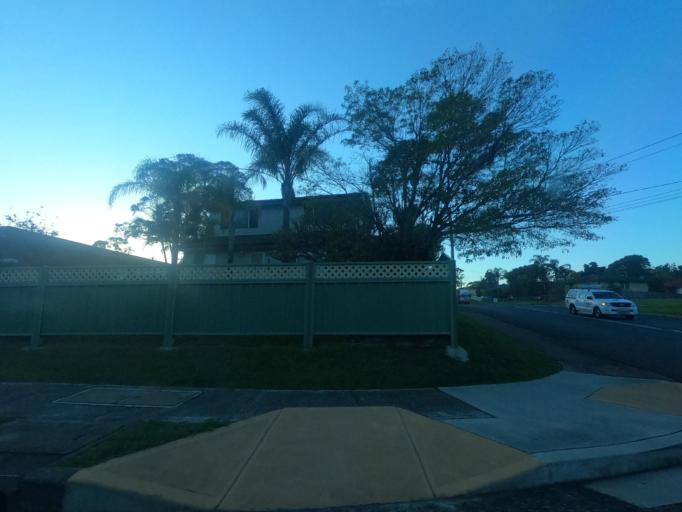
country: AU
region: New South Wales
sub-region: Wollongong
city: Koonawarra
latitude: -34.5044
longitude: 150.8027
